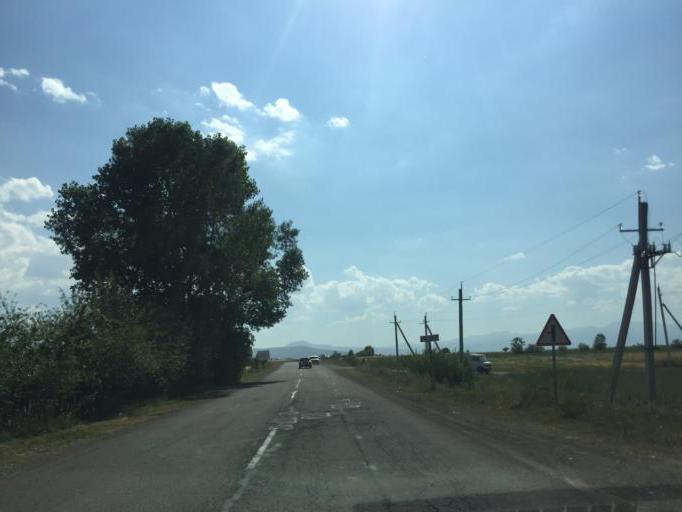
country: AM
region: Geghark'unik'i Marz
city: Tsovinar
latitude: 40.1576
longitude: 45.4490
